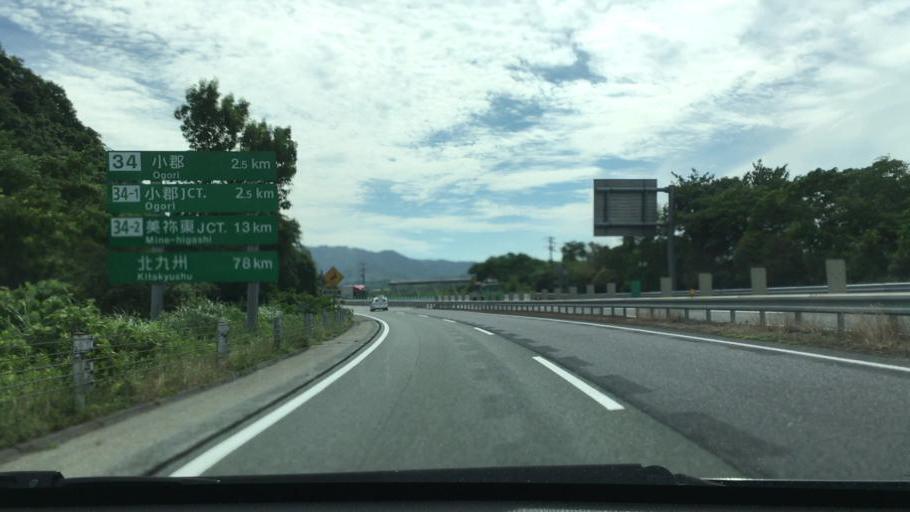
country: JP
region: Yamaguchi
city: Ogori-shimogo
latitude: 34.1327
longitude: 131.4281
